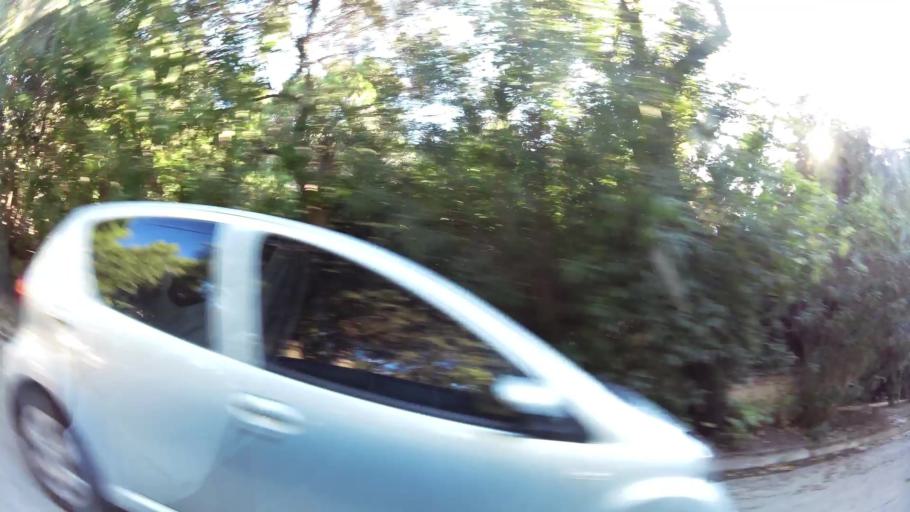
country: GR
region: Attica
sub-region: Nomarchia Athinas
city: Ekali
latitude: 38.1056
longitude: 23.8403
